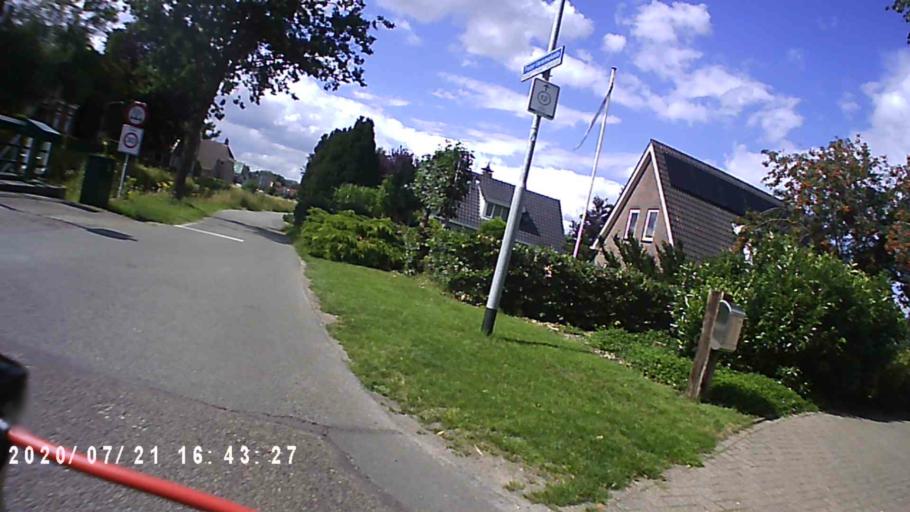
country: NL
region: Groningen
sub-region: Gemeente Hoogezand-Sappemeer
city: Sappemeer
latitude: 53.1044
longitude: 6.7856
